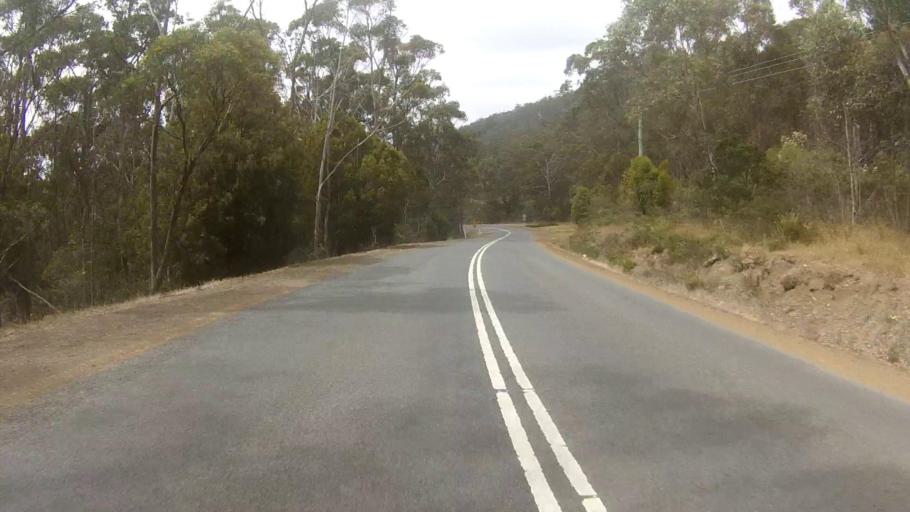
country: AU
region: Tasmania
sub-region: Kingborough
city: Margate
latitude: -42.9990
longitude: 147.2301
